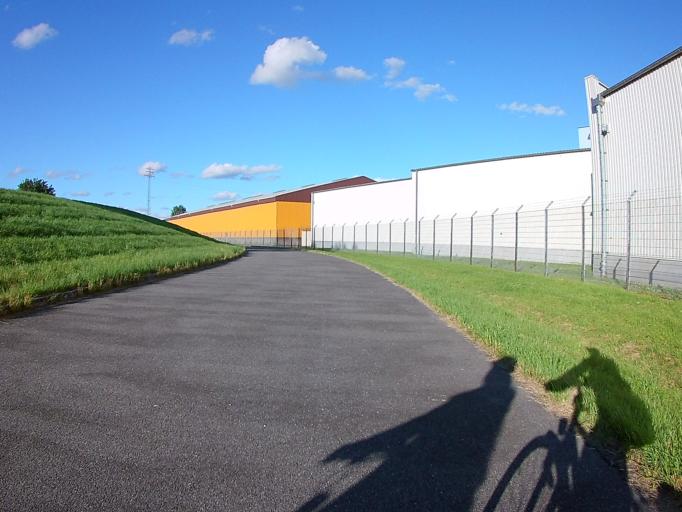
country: DE
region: Hamburg
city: Harburg
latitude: 53.4707
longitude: 9.9770
